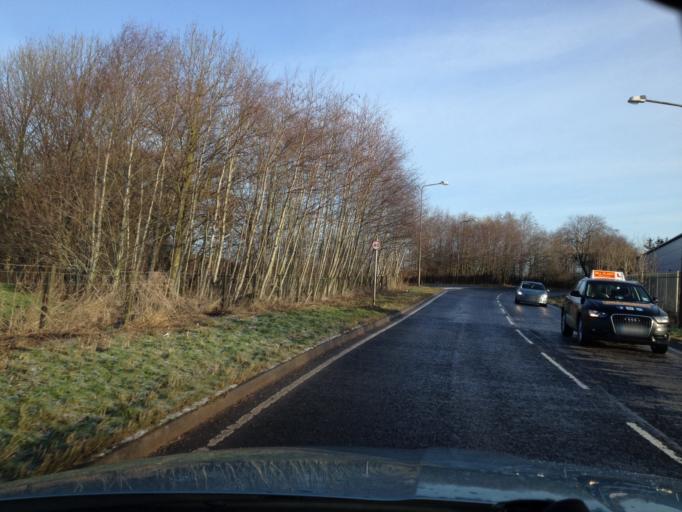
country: GB
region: Scotland
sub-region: West Lothian
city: Bathgate
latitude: 55.8864
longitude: -3.6620
